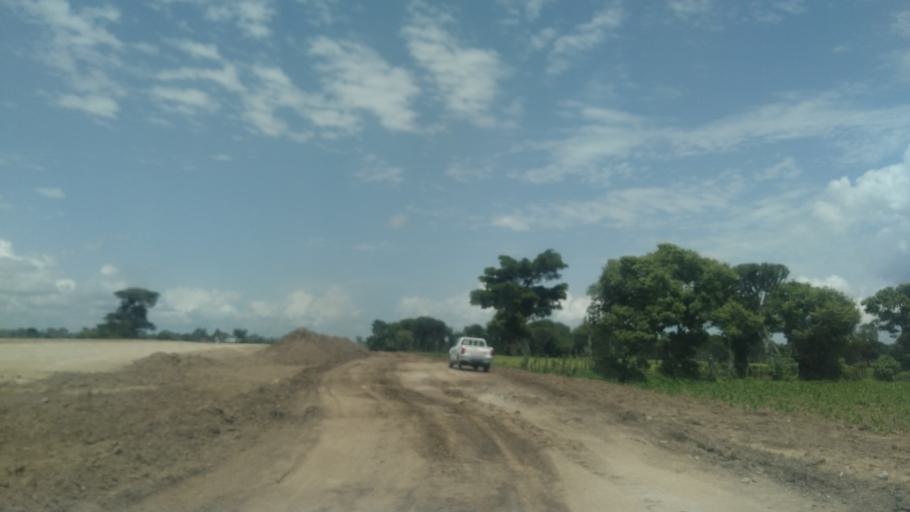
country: ET
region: Oromiya
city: Shashemene
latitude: 7.2833
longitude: 38.6070
